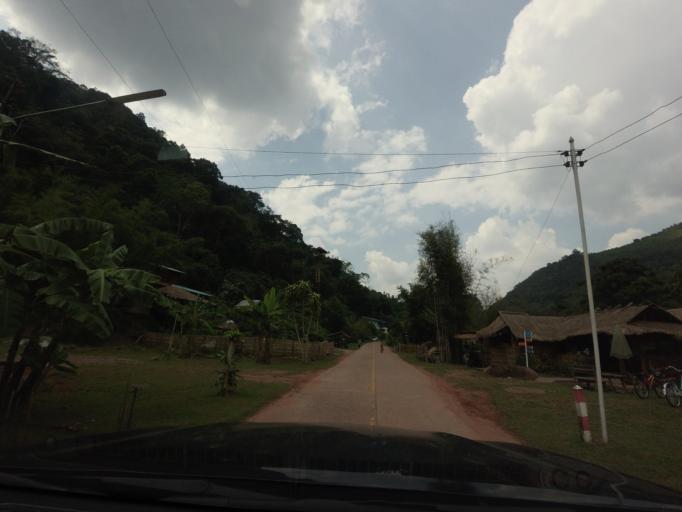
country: TH
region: Nan
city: Bo Kluea
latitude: 19.1924
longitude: 101.1972
